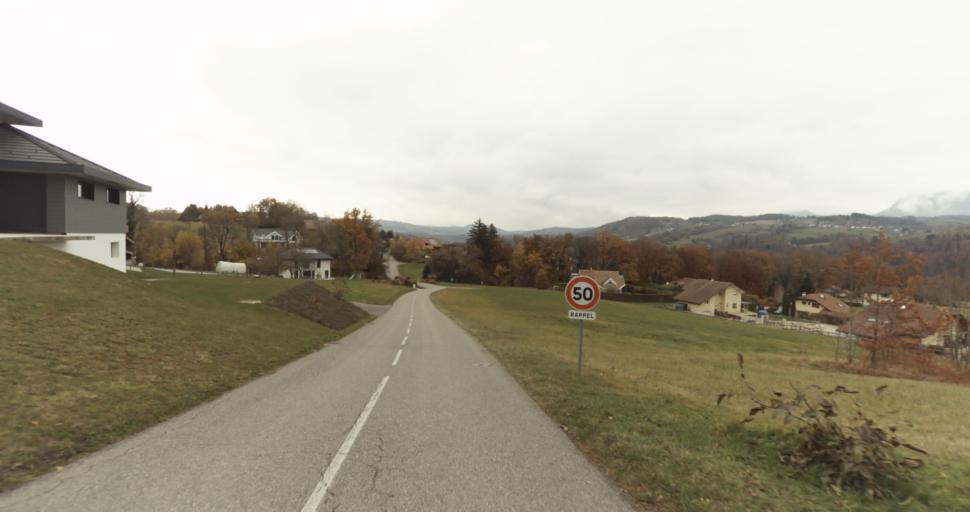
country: FR
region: Rhone-Alpes
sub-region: Departement de la Haute-Savoie
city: Saint-Martin-Bellevue
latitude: 45.9741
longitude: 6.1530
